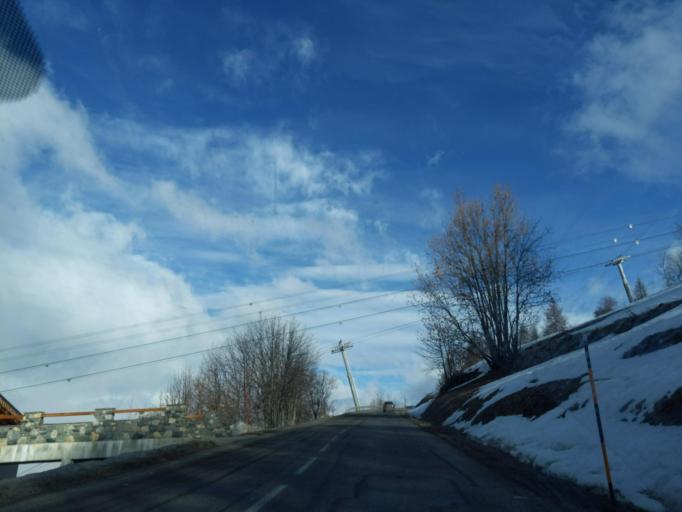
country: FR
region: Rhone-Alpes
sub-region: Departement de la Savoie
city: Belle-Plagne
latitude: 45.5493
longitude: 6.7607
